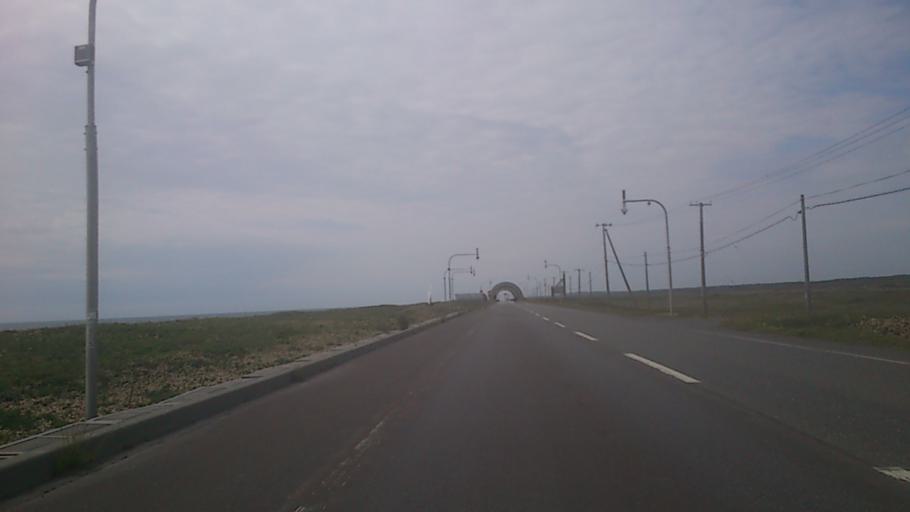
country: JP
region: Hokkaido
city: Makubetsu
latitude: 45.0009
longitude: 141.6822
